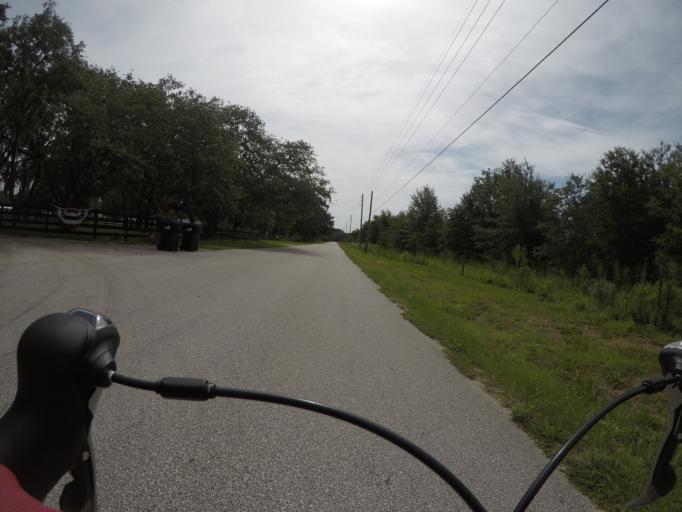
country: US
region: Florida
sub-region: Osceola County
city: Buenaventura Lakes
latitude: 28.3782
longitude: -81.2314
